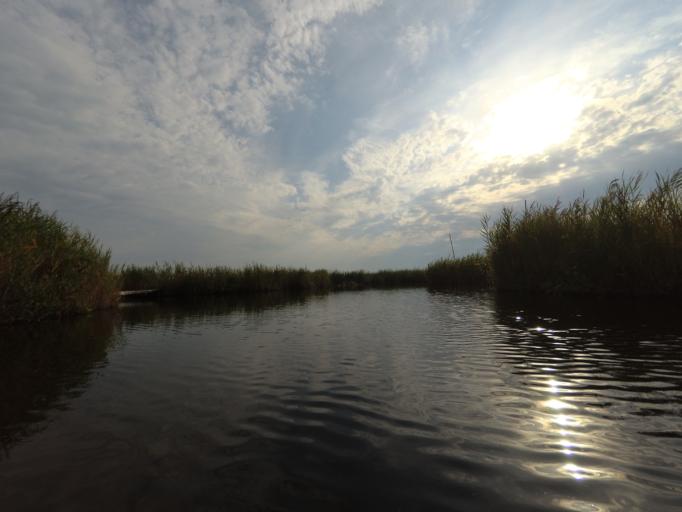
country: NL
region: South Holland
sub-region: Gemeente Nieuwkoop
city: Nieuwkoop
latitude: 52.1469
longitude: 4.8130
